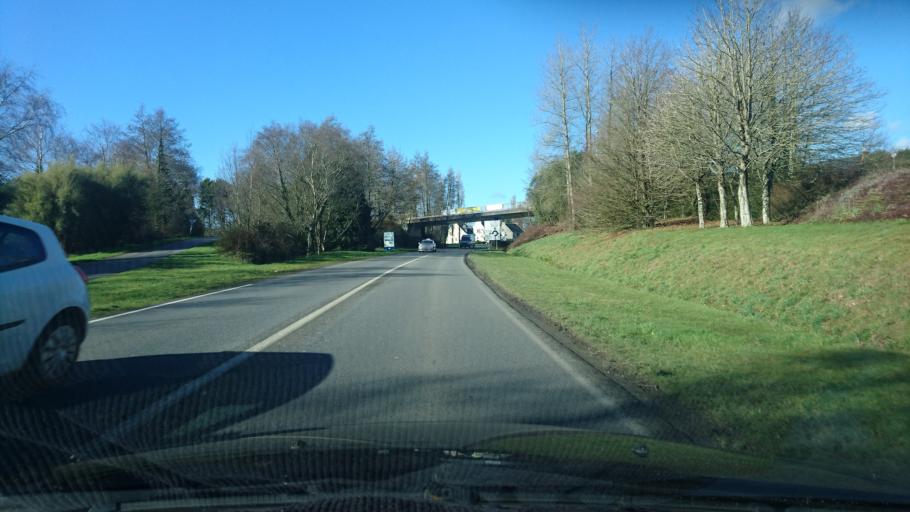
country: FR
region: Brittany
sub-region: Departement du Finistere
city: Saint-Renan
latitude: 48.4335
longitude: -4.6156
